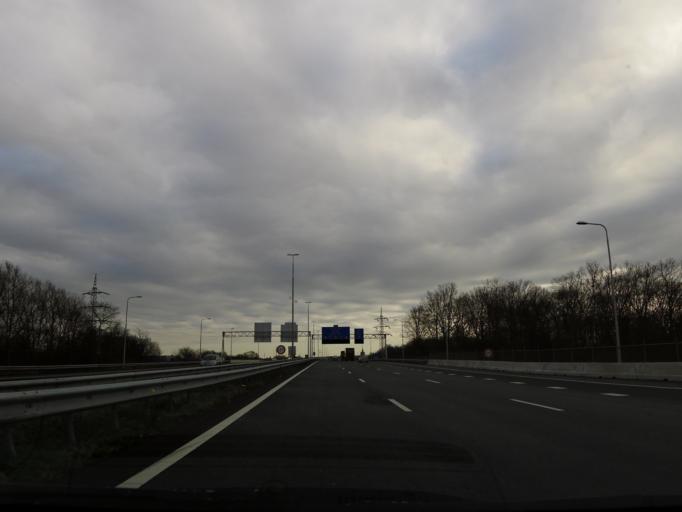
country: NL
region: Limburg
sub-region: Gemeente Beek
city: Beek
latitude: 50.9615
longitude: 5.8018
